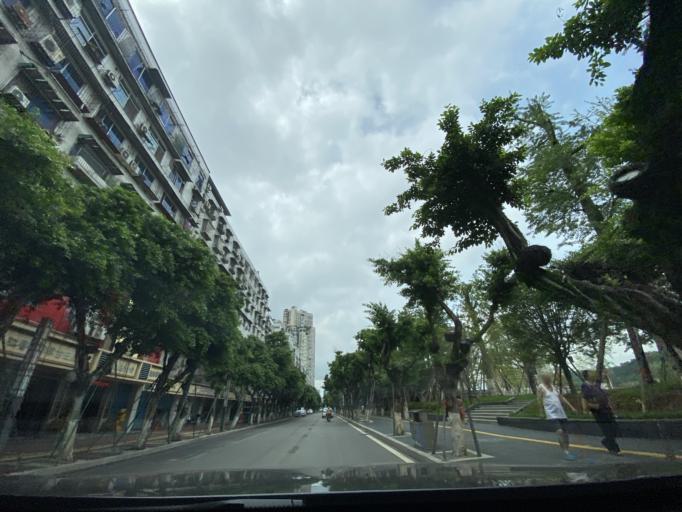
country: CN
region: Sichuan
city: Jiancheng
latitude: 30.3953
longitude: 104.5527
